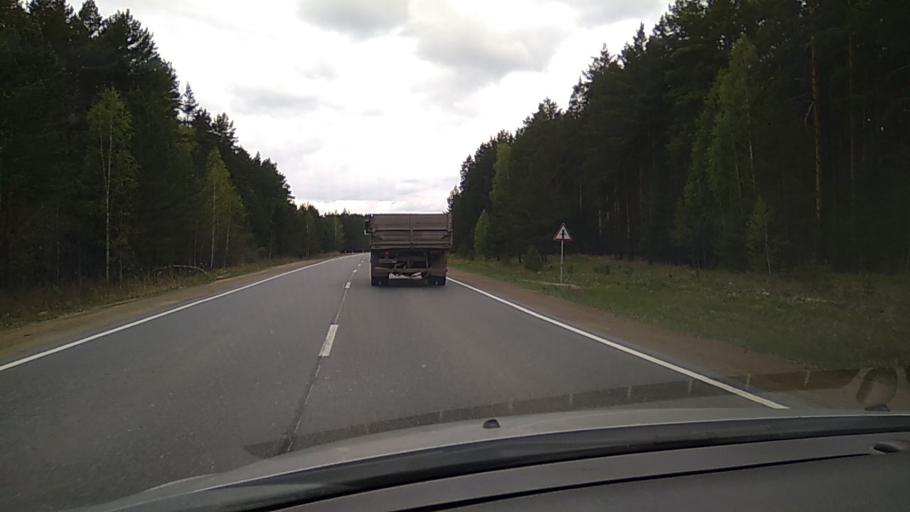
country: RU
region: Kurgan
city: Kataysk
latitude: 56.3002
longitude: 62.3746
